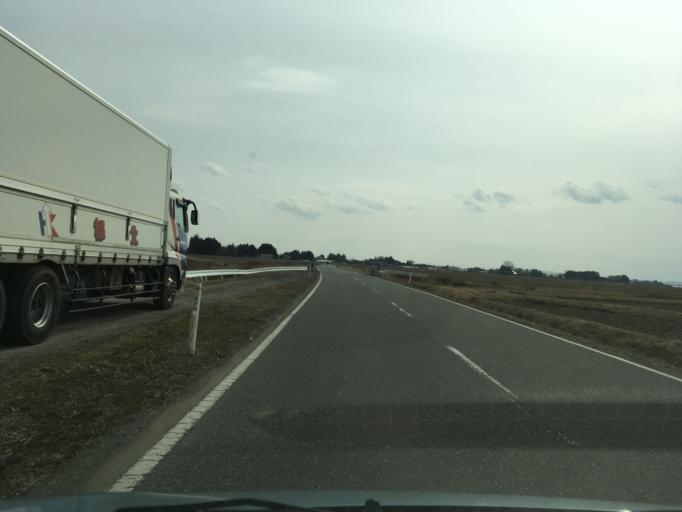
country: JP
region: Miyagi
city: Wakuya
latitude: 38.7276
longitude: 141.2397
